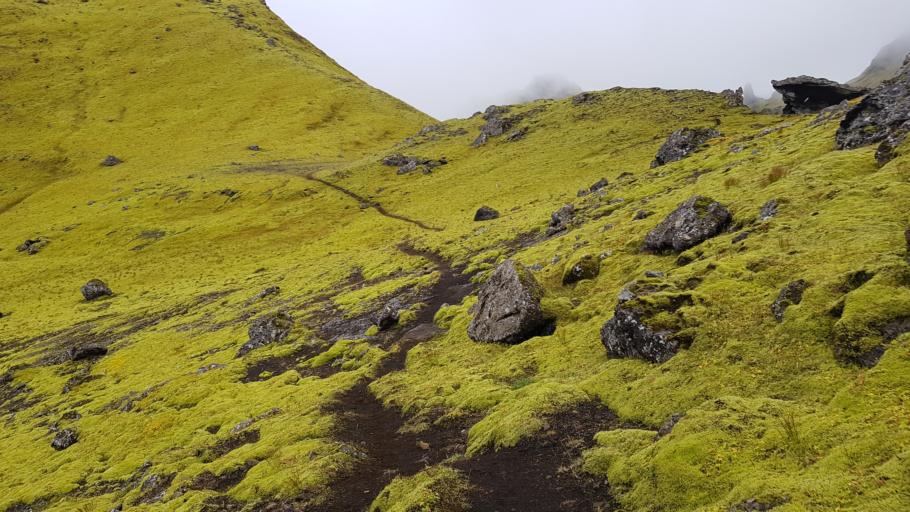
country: IS
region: South
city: Vestmannaeyjar
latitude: 63.5383
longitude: -18.8551
